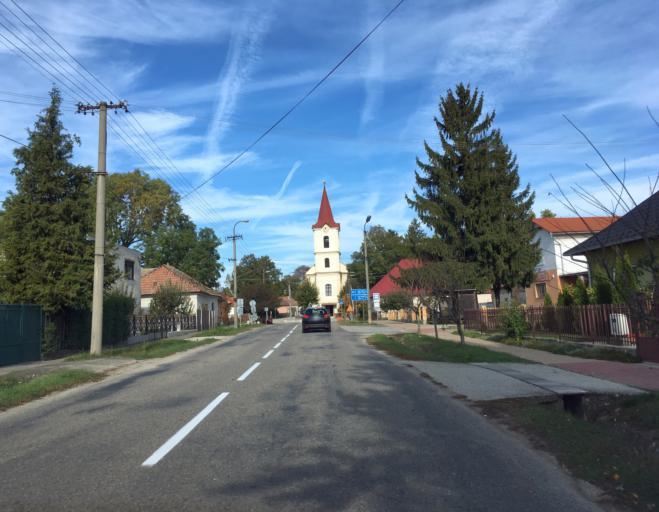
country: SK
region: Nitriansky
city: Svodin
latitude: 48.0161
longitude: 18.4133
